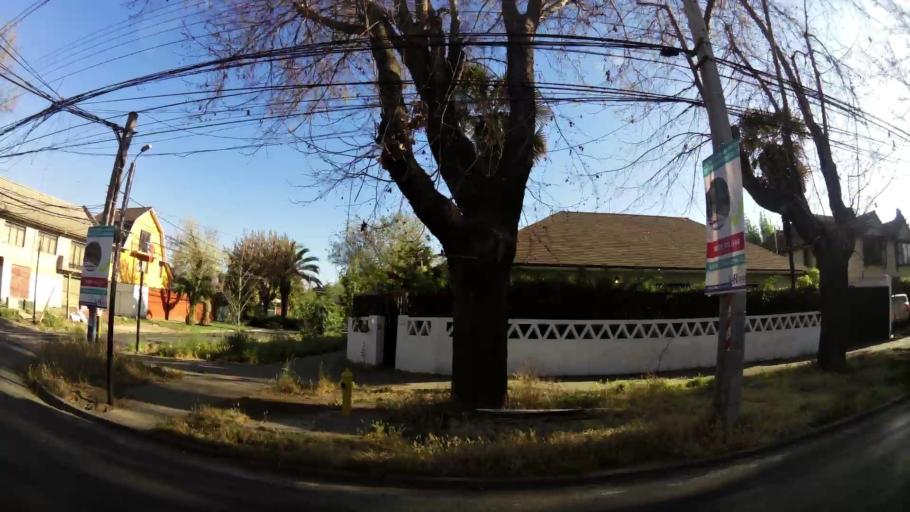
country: CL
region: Santiago Metropolitan
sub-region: Provincia de Santiago
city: Villa Presidente Frei, Nunoa, Santiago, Chile
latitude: -33.4475
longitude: -70.5678
